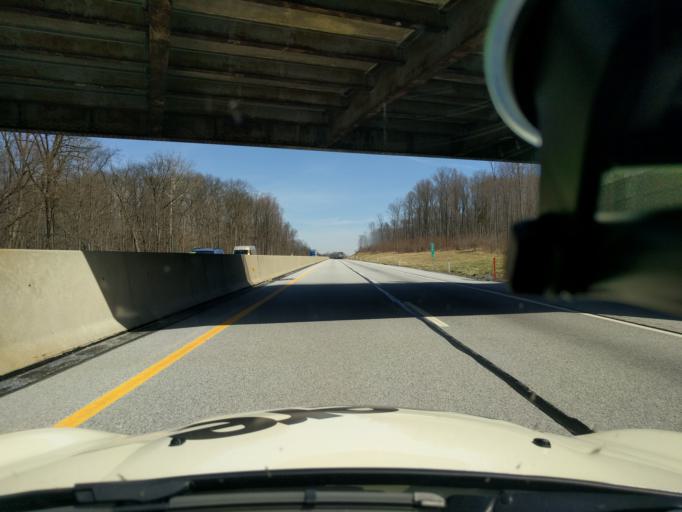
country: US
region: Pennsylvania
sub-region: Lebanon County
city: Campbelltown
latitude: 40.2188
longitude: -76.5273
